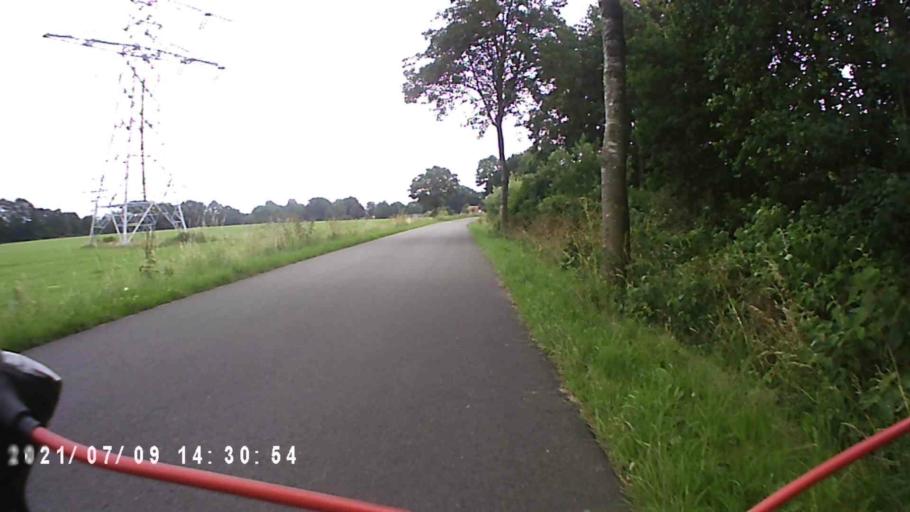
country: DE
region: Lower Saxony
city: Weener
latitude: 53.1272
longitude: 7.3125
